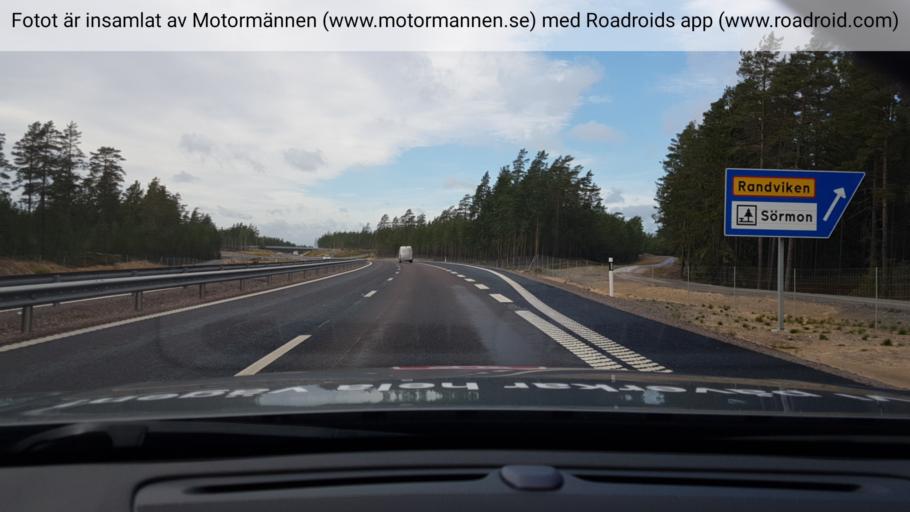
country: SE
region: Vaermland
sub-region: Kils Kommun
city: Kil
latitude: 59.3848
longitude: 13.3486
